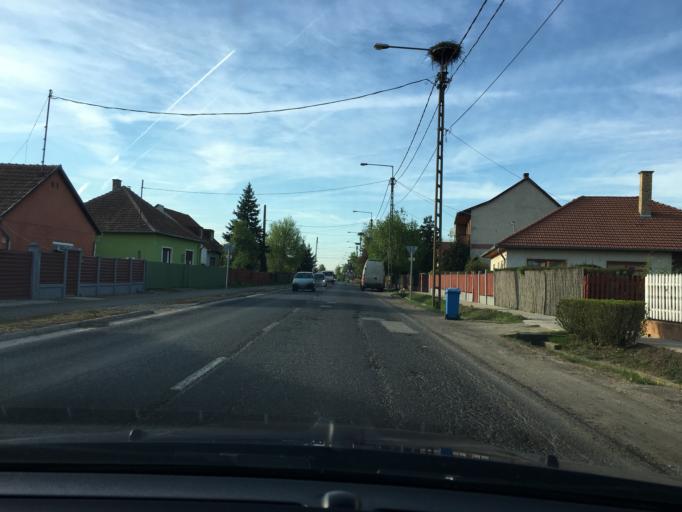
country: HU
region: Hajdu-Bihar
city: Berettyoujfalu
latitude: 47.1934
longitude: 21.5419
